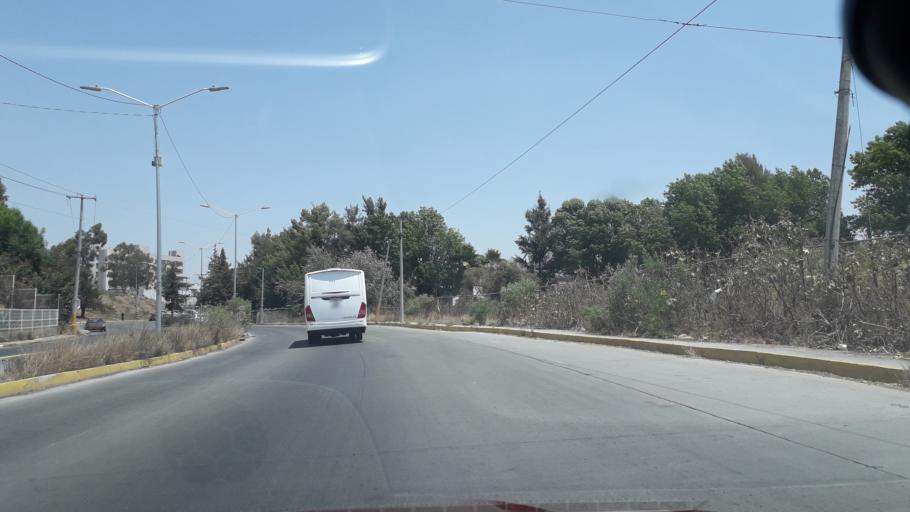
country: MX
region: Puebla
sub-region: Puebla
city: Galaxia la Calera
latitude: 19.0050
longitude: -98.1839
